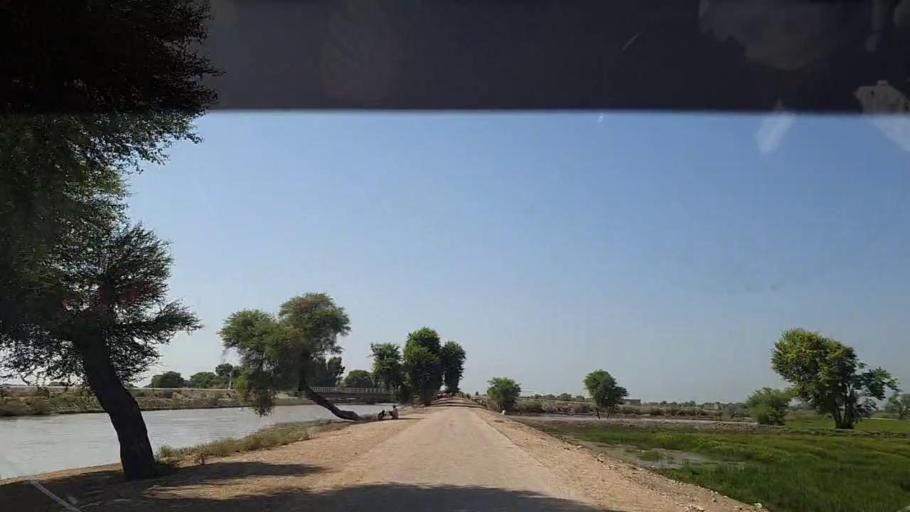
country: PK
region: Sindh
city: Ghauspur
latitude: 28.1997
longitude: 69.0427
